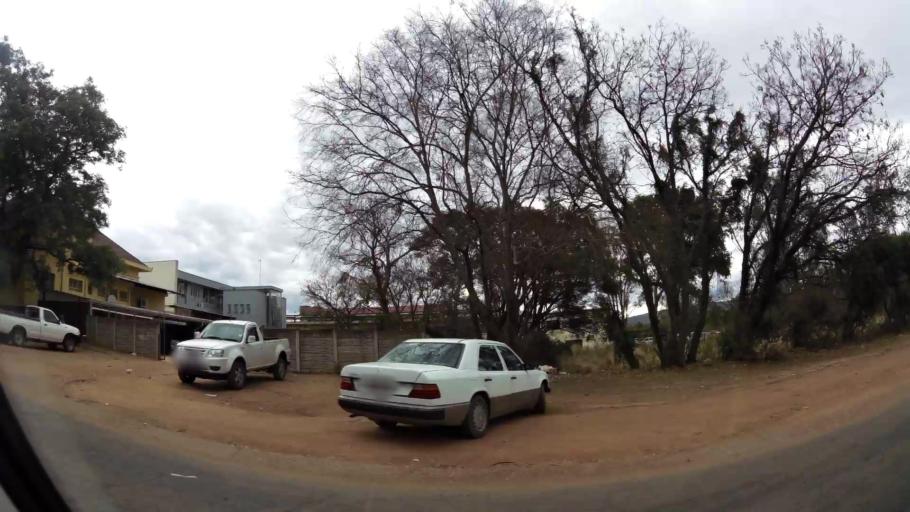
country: ZA
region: Limpopo
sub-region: Waterberg District Municipality
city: Modimolle
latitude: -24.7028
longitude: 28.4092
